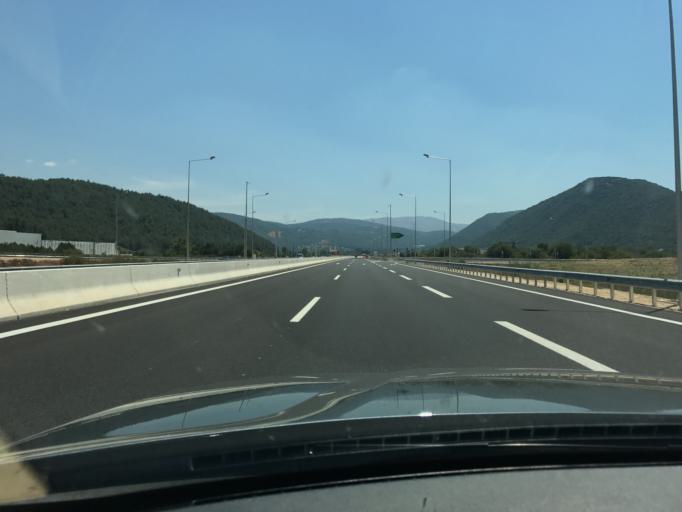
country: GR
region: Epirus
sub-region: Nomos Ioanninon
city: Agia Kyriaki
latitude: 39.5339
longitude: 20.8718
